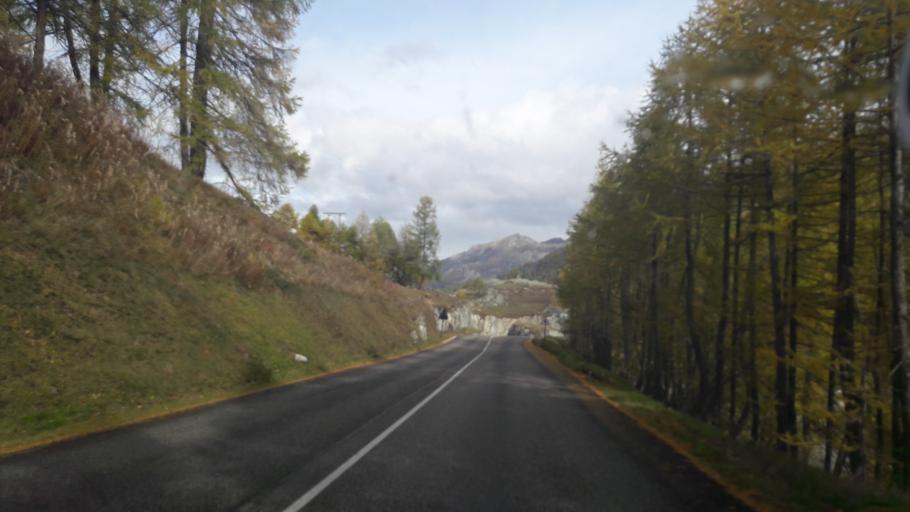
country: FR
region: Rhone-Alpes
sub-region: Departement de la Savoie
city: Tignes
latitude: 45.4911
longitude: 6.9253
